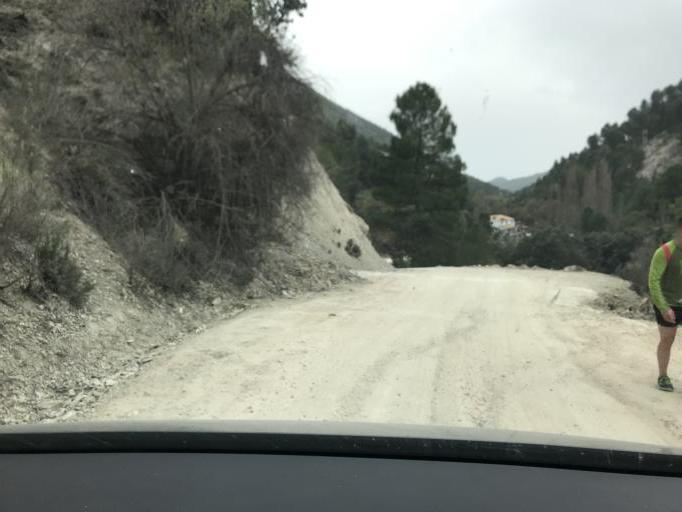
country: ES
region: Andalusia
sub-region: Provincia de Granada
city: Castril
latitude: 37.8786
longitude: -2.7559
